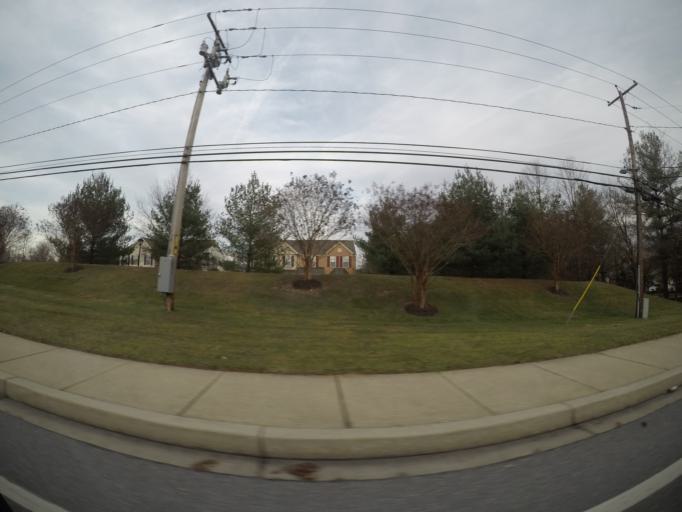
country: US
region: Maryland
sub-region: Howard County
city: Ilchester
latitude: 39.2031
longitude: -76.7953
